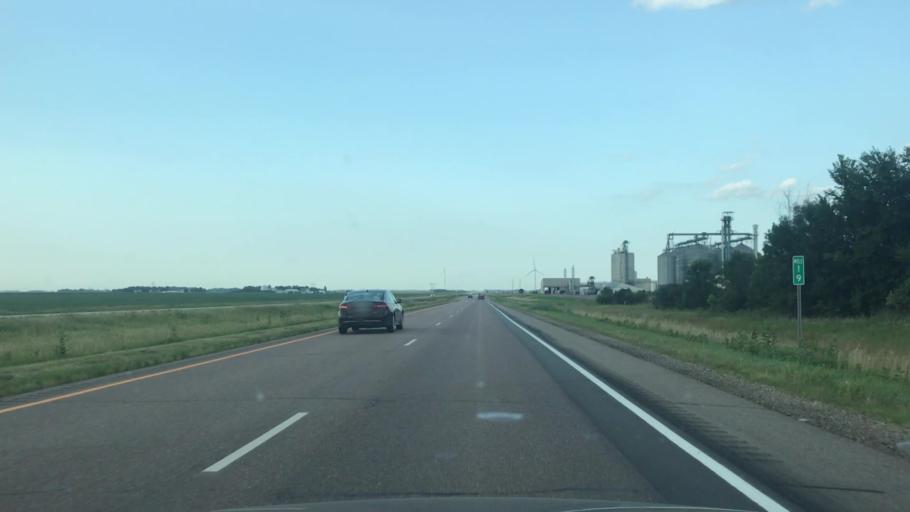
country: US
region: Minnesota
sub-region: Nobles County
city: Worthington
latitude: 43.7019
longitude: -95.4664
